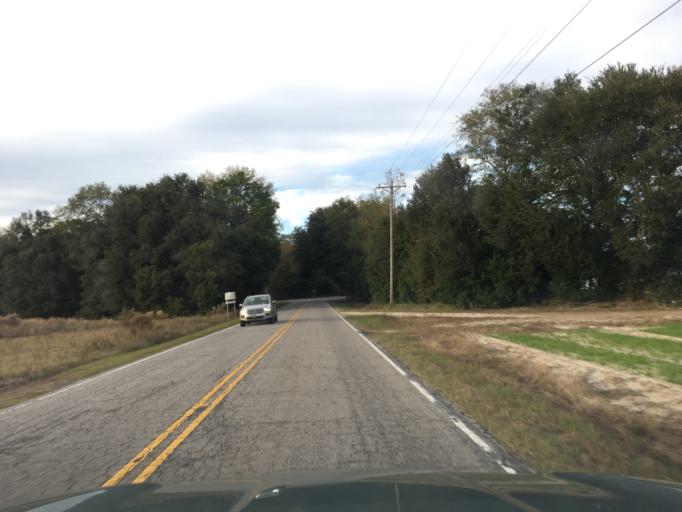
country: US
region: South Carolina
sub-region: Lexington County
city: Leesville
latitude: 33.7557
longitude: -81.3671
